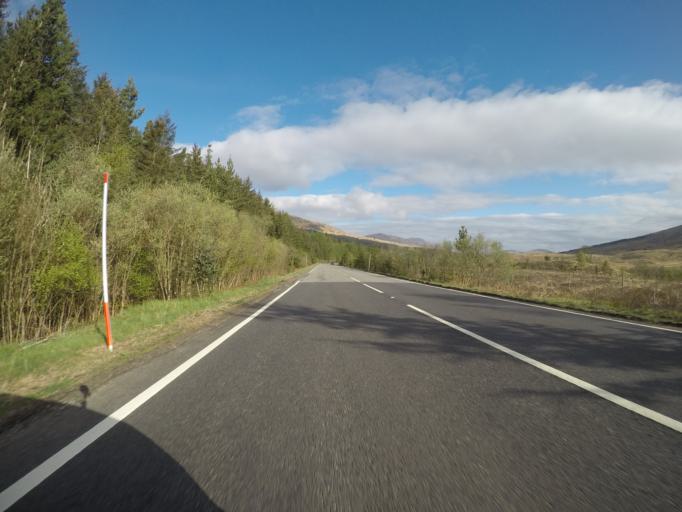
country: GB
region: Scotland
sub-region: Highland
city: Spean Bridge
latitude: 56.5019
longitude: -4.7648
